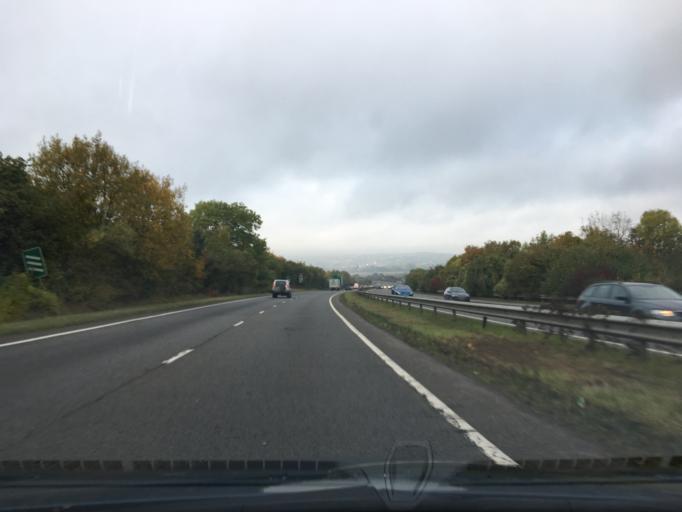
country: GB
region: England
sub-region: Surrey
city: Seale
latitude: 51.2255
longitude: -0.7293
